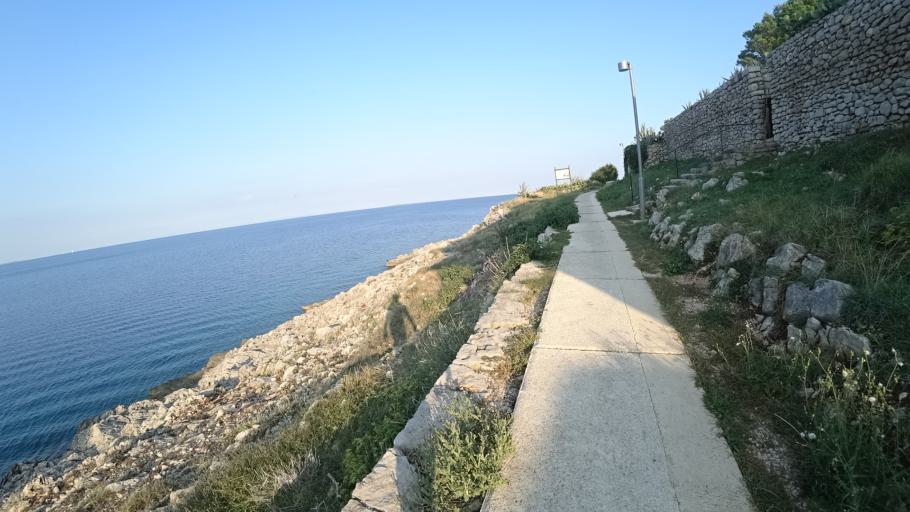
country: HR
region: Primorsko-Goranska
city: Mali Losinj
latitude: 44.5281
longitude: 14.4863
